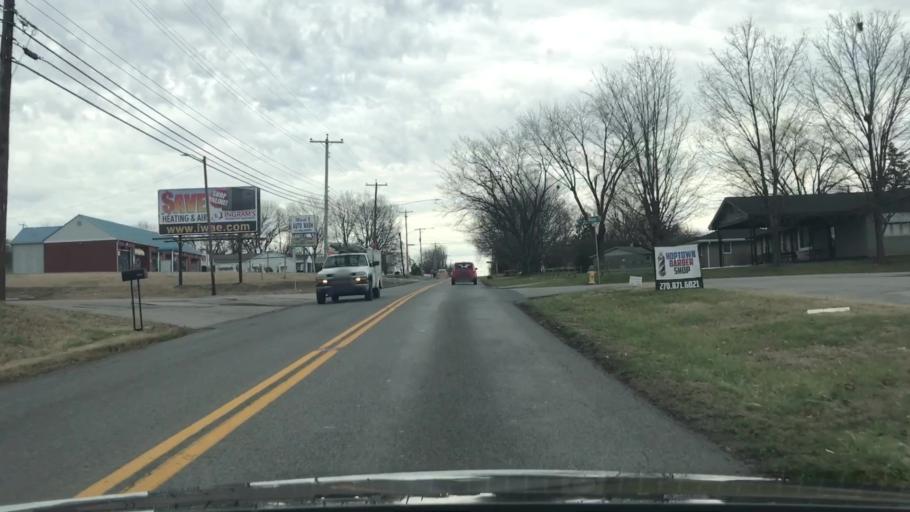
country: US
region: Kentucky
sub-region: Christian County
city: Hopkinsville
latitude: 36.8606
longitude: -87.5129
